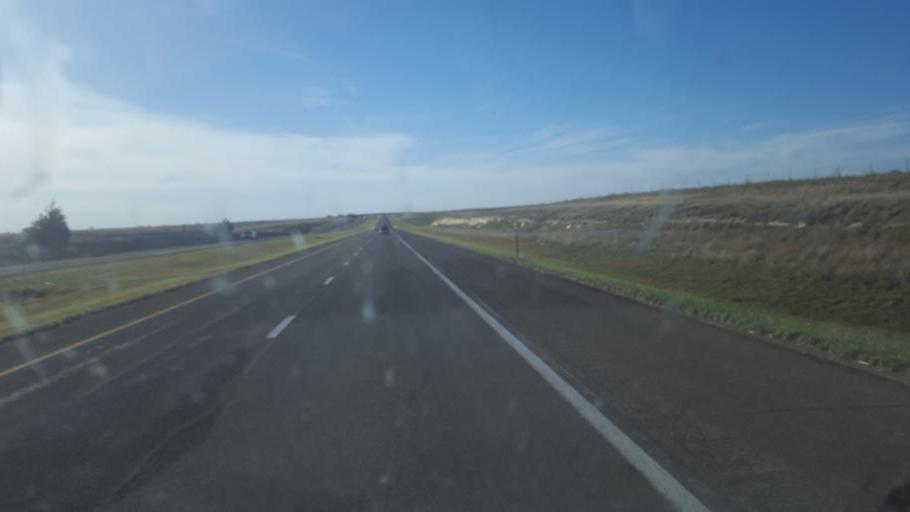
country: US
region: Kansas
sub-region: Ellis County
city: Ellis
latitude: 38.9395
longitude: -99.4870
